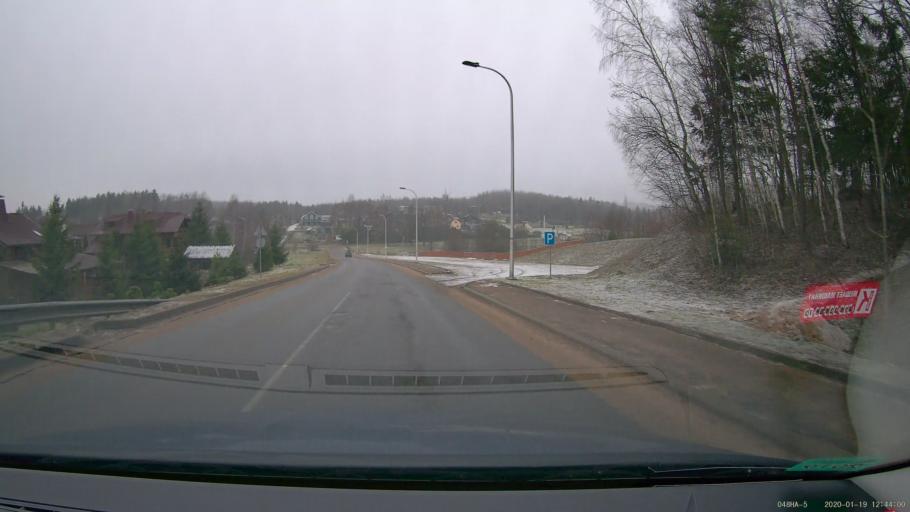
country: BY
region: Minsk
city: Lahoysk
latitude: 54.1787
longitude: 27.8090
